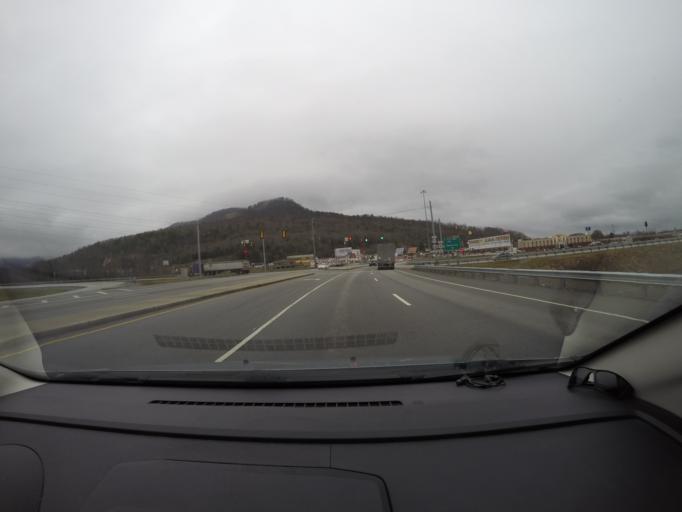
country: US
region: Tennessee
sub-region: Marion County
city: Kimball
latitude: 35.0406
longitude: -85.6903
